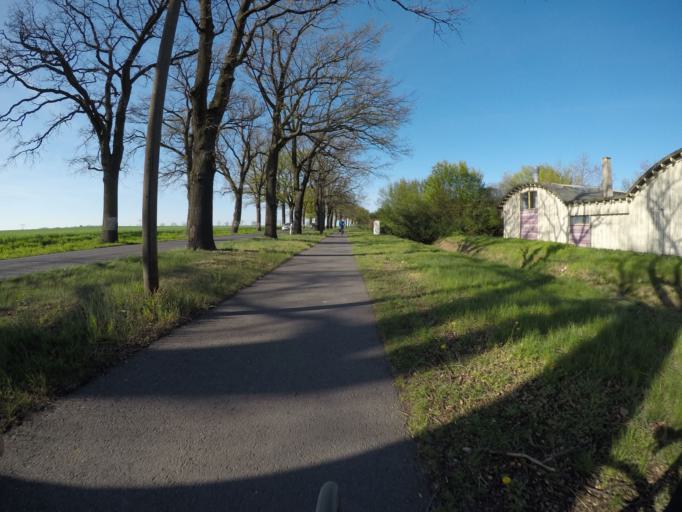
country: DE
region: Brandenburg
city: Schoneiche
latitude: 52.4952
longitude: 13.6989
